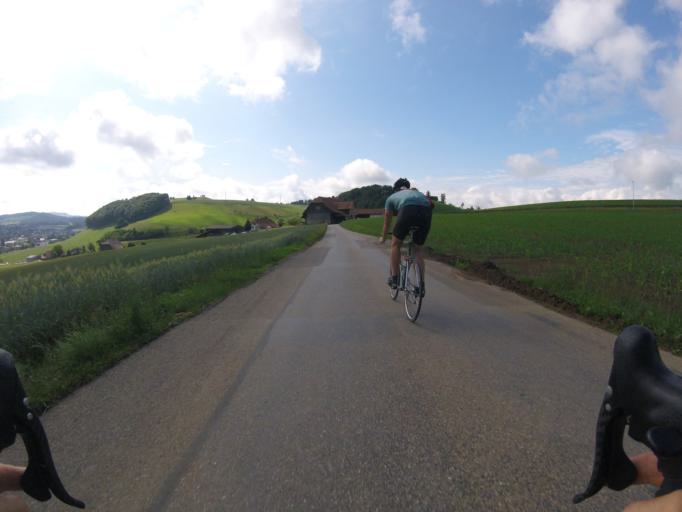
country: CH
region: Bern
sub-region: Bern-Mittelland District
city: Worb
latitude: 46.9295
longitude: 7.5477
